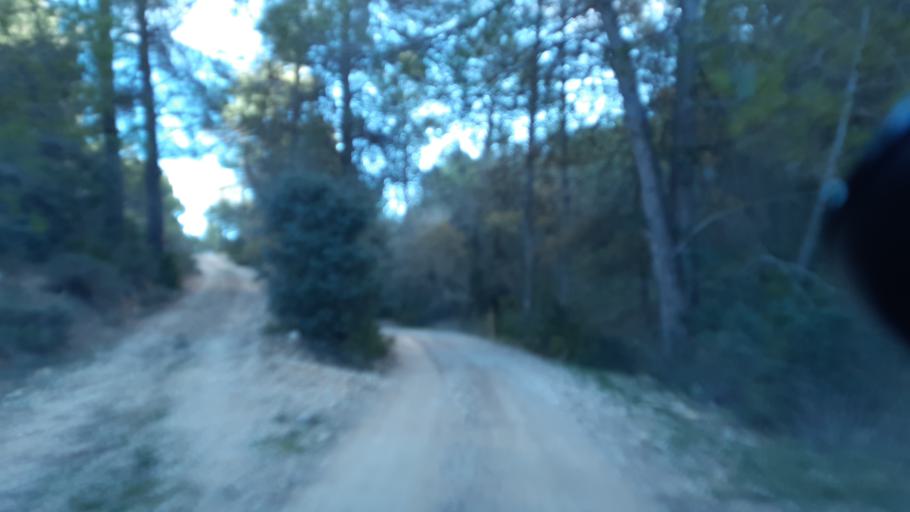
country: ES
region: Aragon
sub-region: Provincia de Teruel
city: Valderrobres
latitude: 40.8487
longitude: 0.2144
